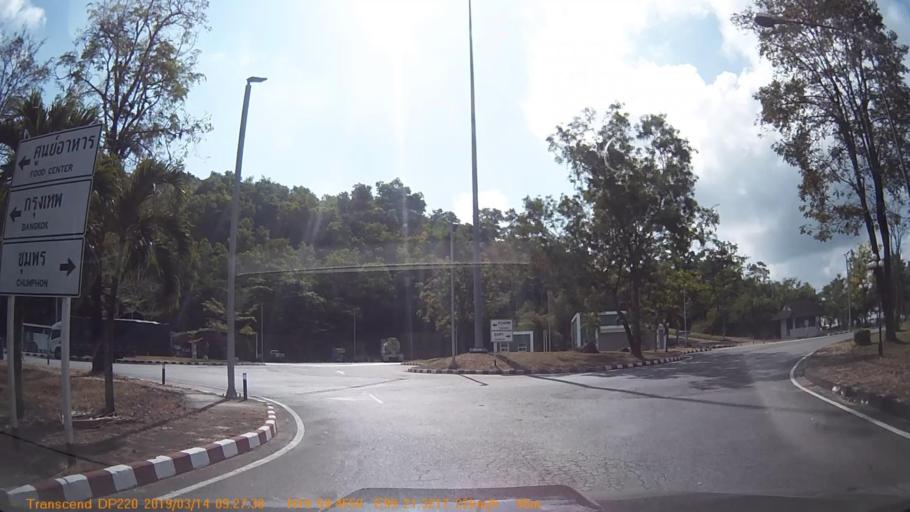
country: TH
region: Prachuap Khiri Khan
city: Bang Saphan Noi
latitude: 10.9914
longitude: 99.3561
